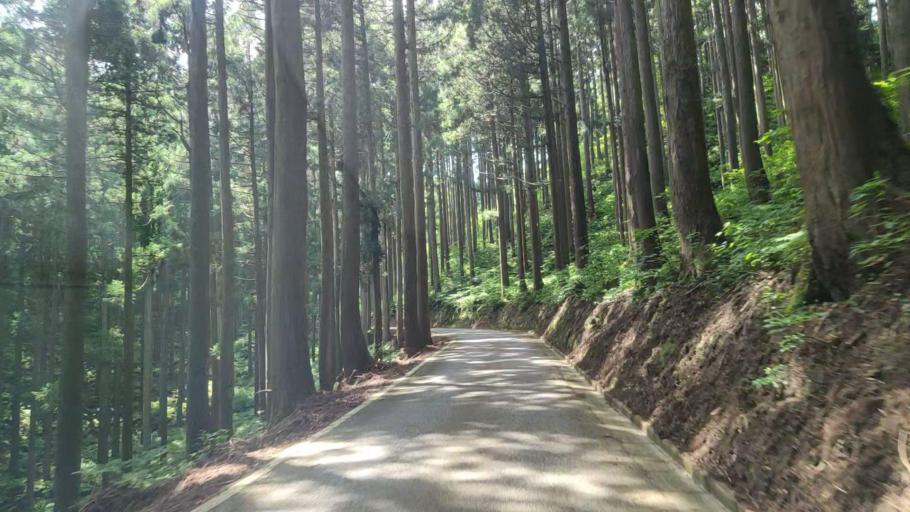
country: JP
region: Ishikawa
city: Komatsu
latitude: 36.2799
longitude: 136.5322
